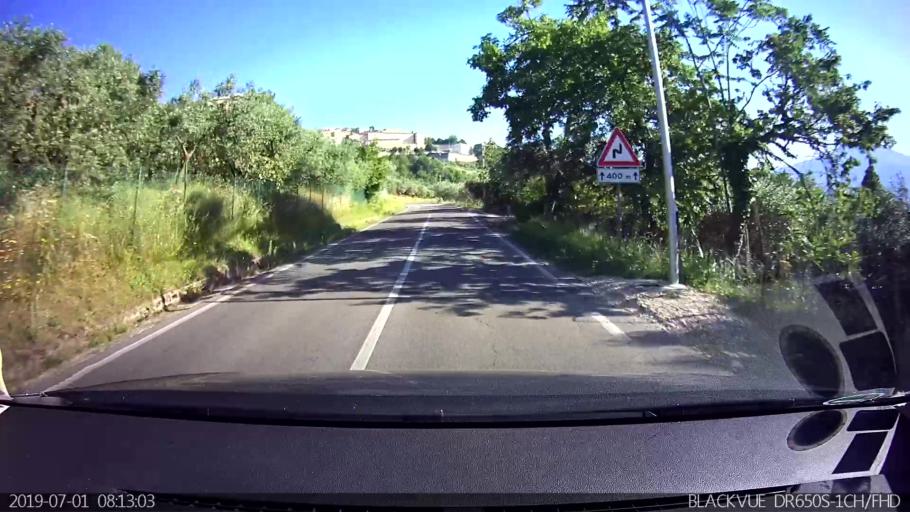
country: IT
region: Latium
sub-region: Provincia di Frosinone
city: Veroli
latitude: 41.6875
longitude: 13.4227
